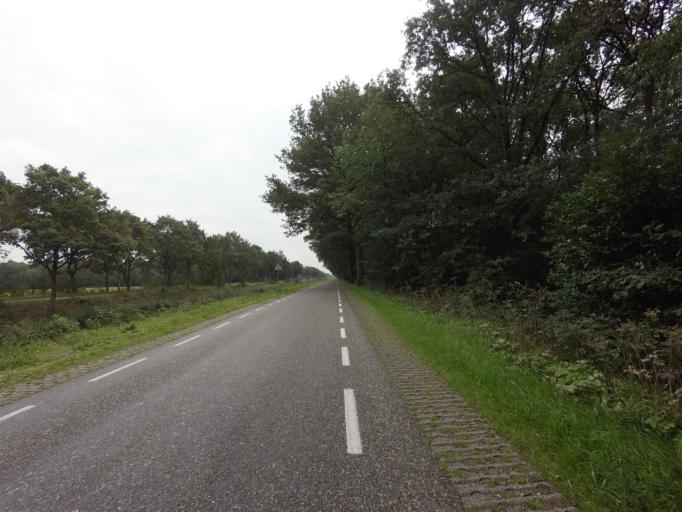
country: NL
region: Drenthe
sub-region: Gemeente Westerveld
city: Dwingeloo
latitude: 52.9034
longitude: 6.4668
